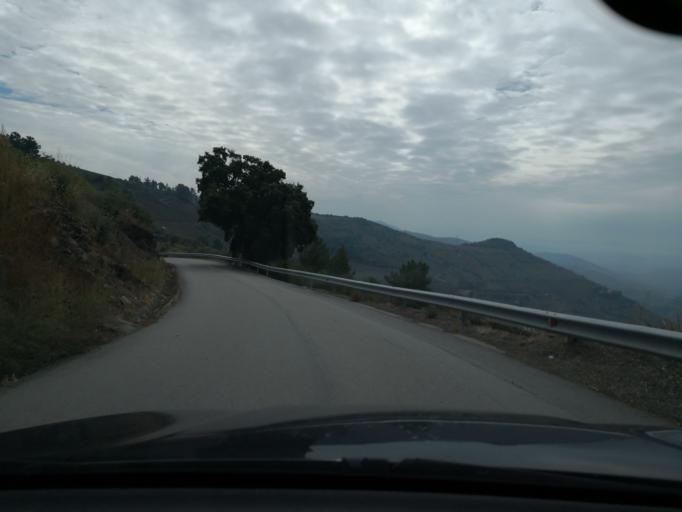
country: PT
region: Vila Real
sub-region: Peso da Regua
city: Peso da Regua
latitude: 41.1980
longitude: -7.7305
